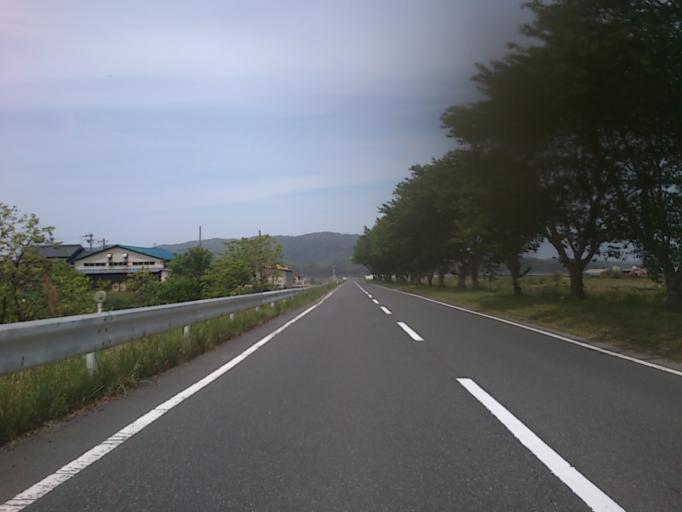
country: JP
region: Kyoto
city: Miyazu
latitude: 35.6608
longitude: 135.0867
